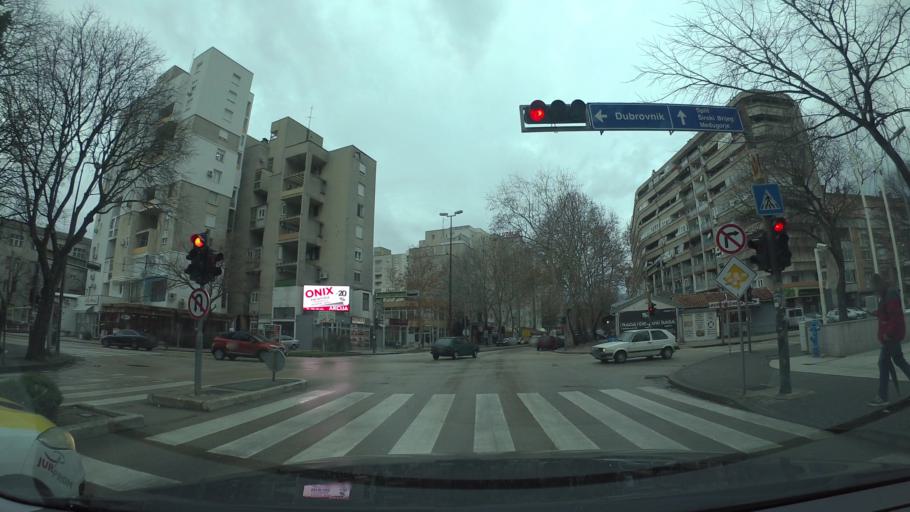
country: BA
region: Federation of Bosnia and Herzegovina
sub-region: Hercegovacko-Bosanski Kanton
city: Mostar
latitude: 43.3478
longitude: 17.8045
